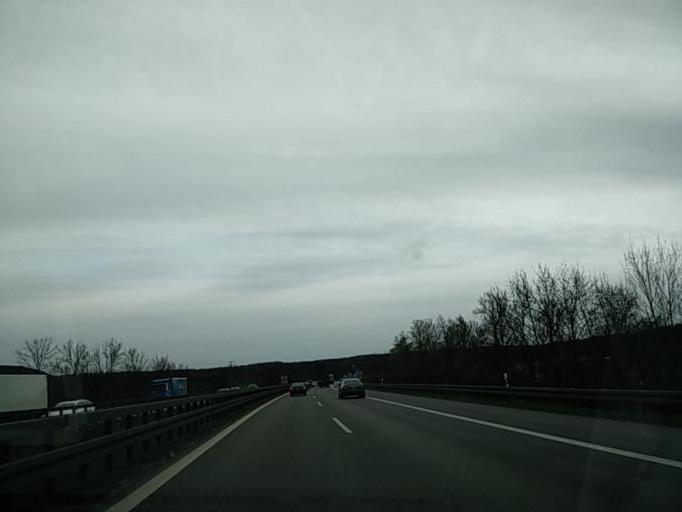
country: DE
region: Baden-Wuerttemberg
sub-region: Regierungsbezirk Stuttgart
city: Gartringen
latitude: 48.6280
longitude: 8.9139
